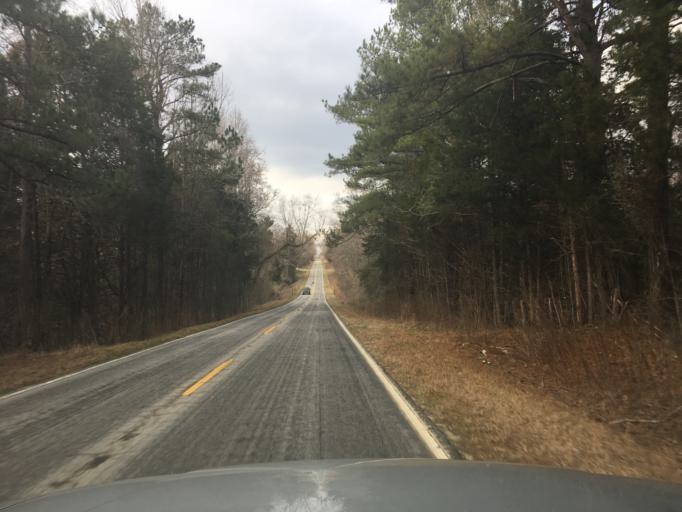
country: US
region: South Carolina
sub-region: Abbeville County
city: Due West
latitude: 34.2586
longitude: -82.4166
